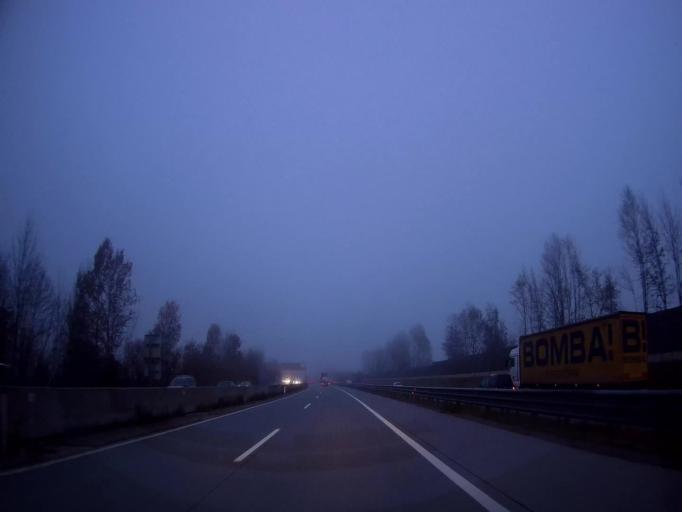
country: AT
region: Salzburg
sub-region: Politischer Bezirk Salzburg-Umgebung
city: Grodig
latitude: 47.7648
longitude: 12.9968
